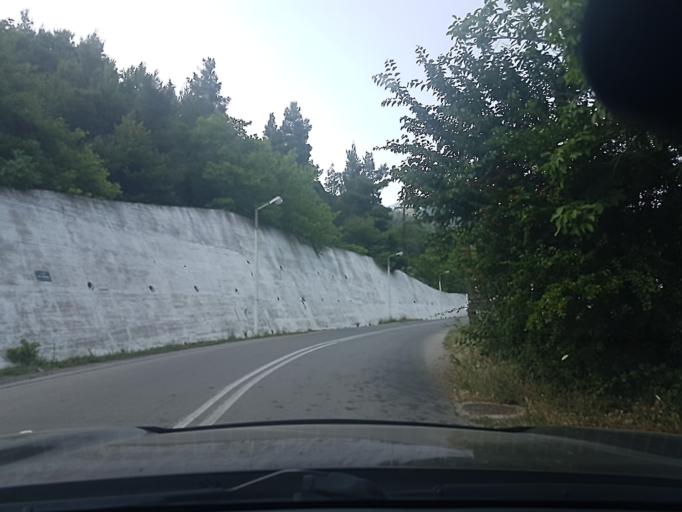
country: GR
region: Central Greece
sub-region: Nomos Evvoias
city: Yimnon
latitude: 38.5805
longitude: 23.8357
